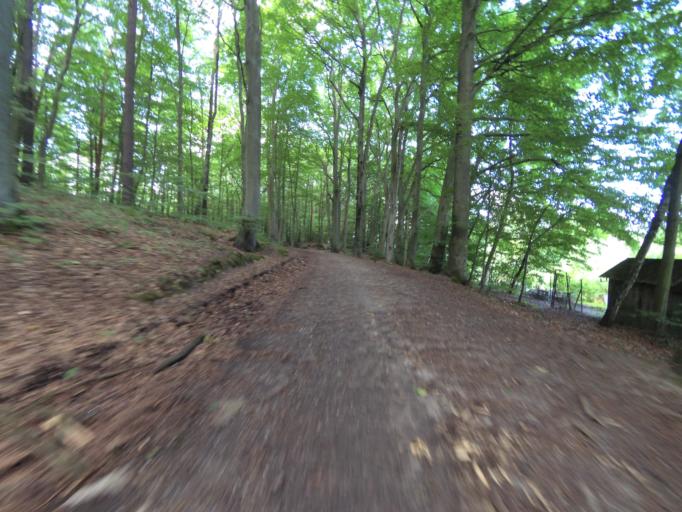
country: PL
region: Pomeranian Voivodeship
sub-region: Gdynia
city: Wielki Kack
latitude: 54.4916
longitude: 18.5062
